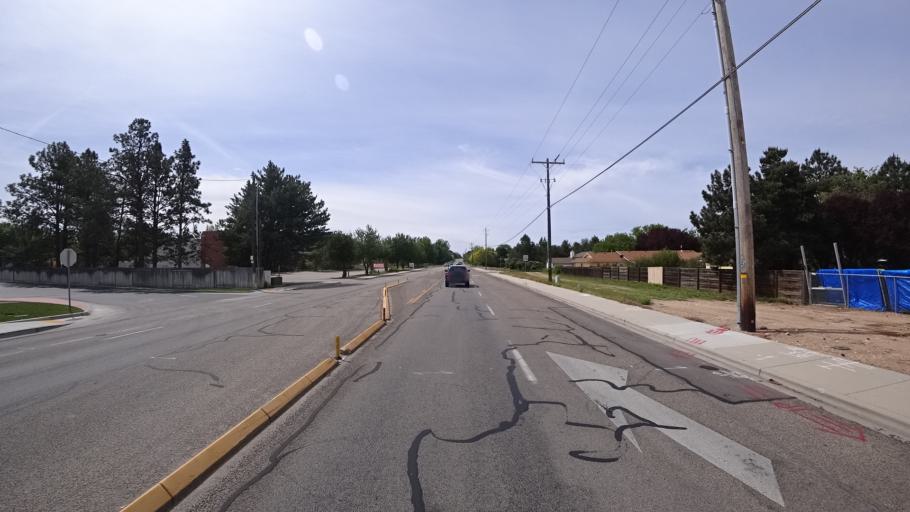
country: US
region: Idaho
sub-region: Ada County
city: Meridian
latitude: 43.5752
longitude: -116.3142
